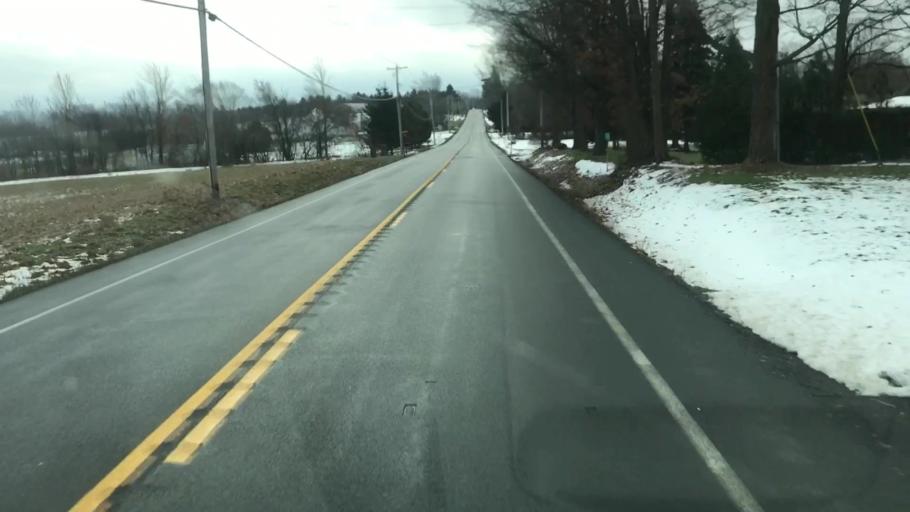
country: US
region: New York
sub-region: Onondaga County
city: Skaneateles
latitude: 42.8449
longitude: -76.3867
